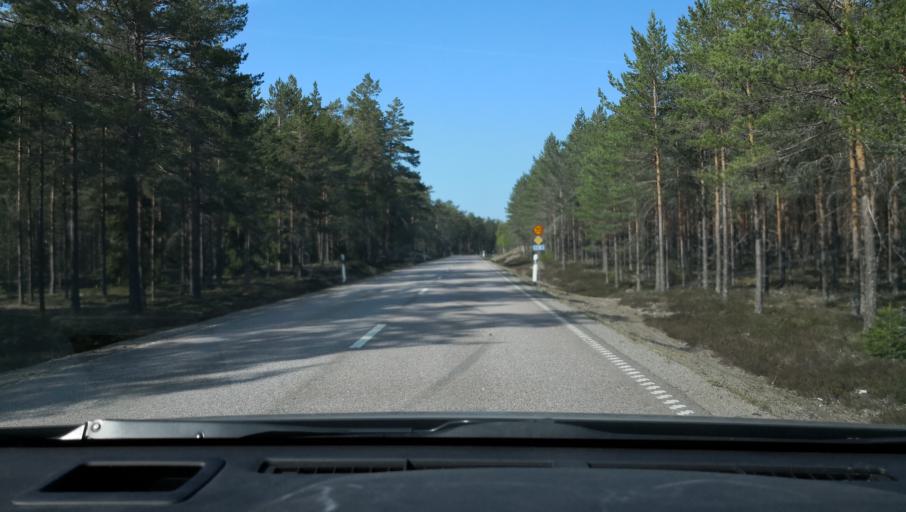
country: SE
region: Uppsala
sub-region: Heby Kommun
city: Heby
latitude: 60.0520
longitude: 16.8662
